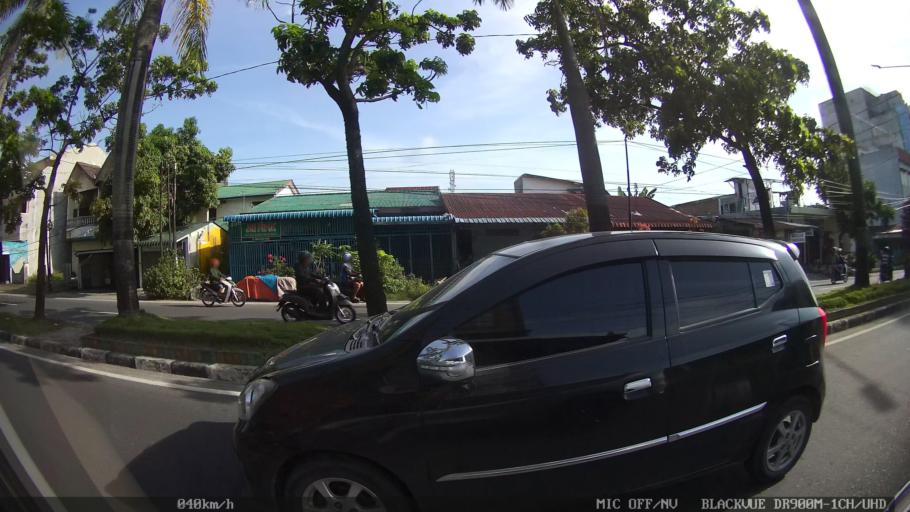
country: ID
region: North Sumatra
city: Medan
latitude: 3.6071
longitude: 98.6627
